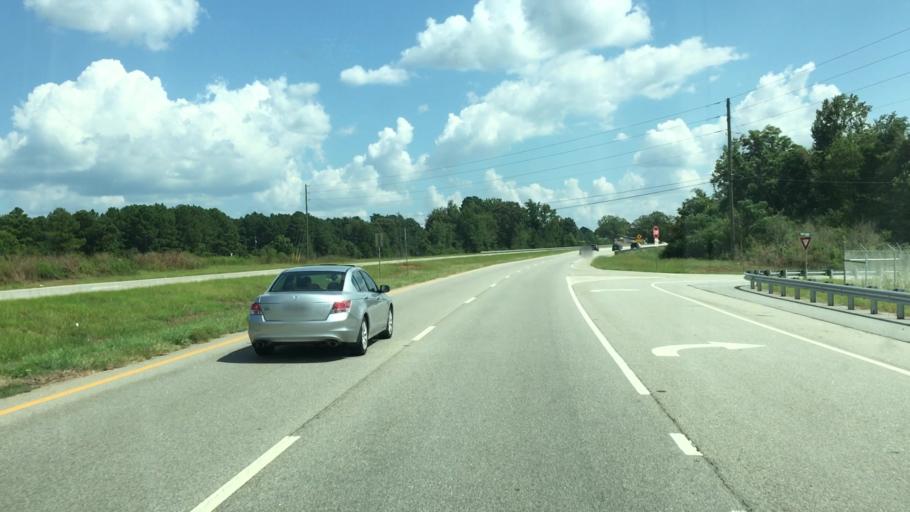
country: US
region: Georgia
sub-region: Putnam County
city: Eatonton
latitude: 33.2891
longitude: -83.3733
